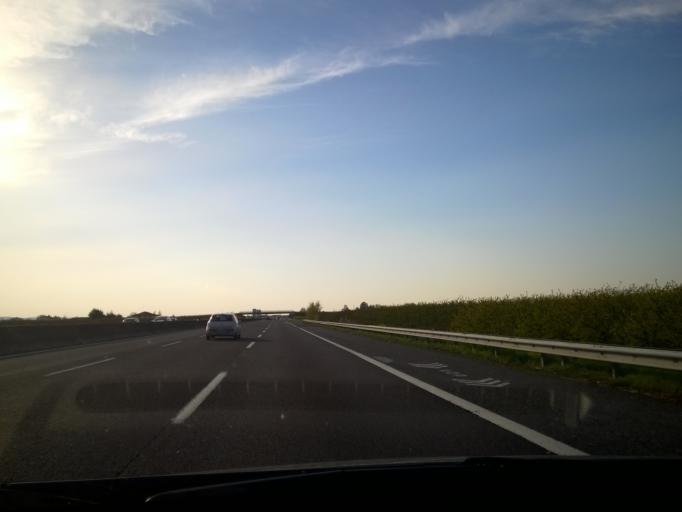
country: IT
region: Emilia-Romagna
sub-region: Provincia di Bologna
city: Bubano
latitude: 44.3717
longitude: 11.7674
